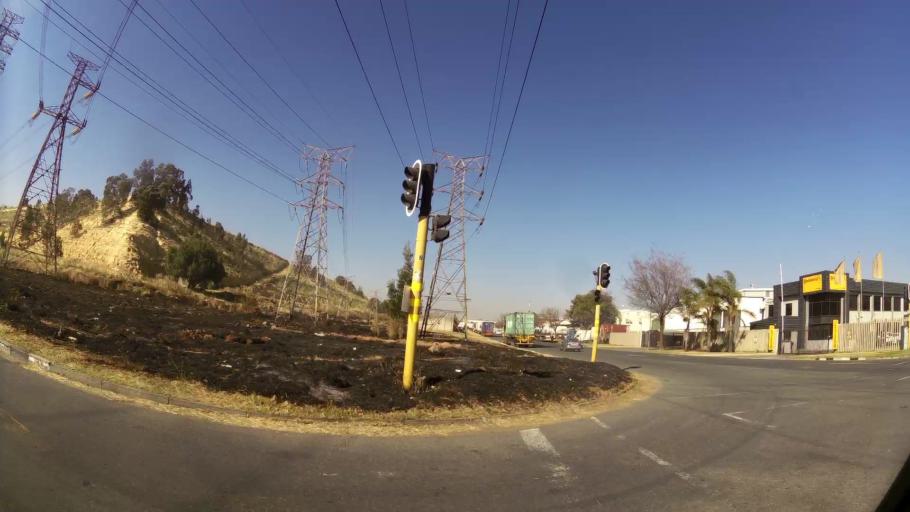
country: ZA
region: Gauteng
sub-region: City of Johannesburg Metropolitan Municipality
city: Johannesburg
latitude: -26.2280
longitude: 28.0937
